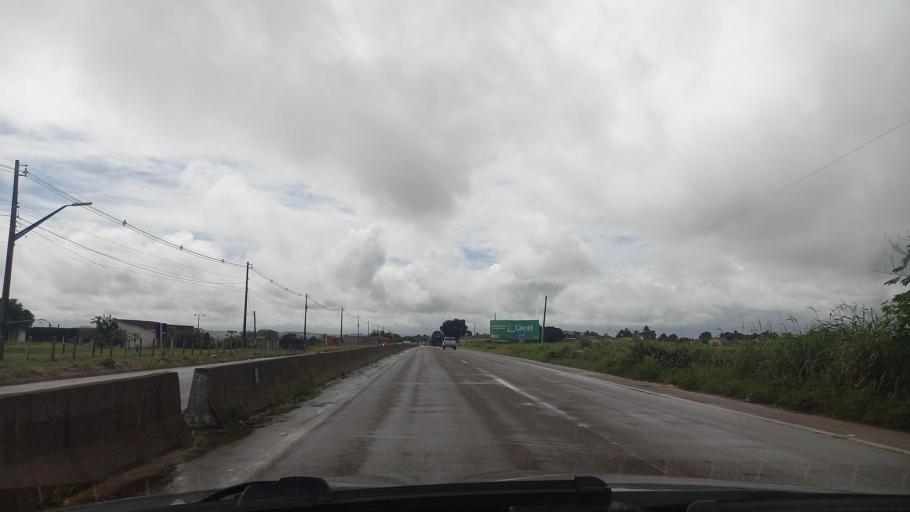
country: BR
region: Alagoas
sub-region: Limoeiro De Anadia
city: Limoeiro de Anadia
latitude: -9.7614
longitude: -36.5295
